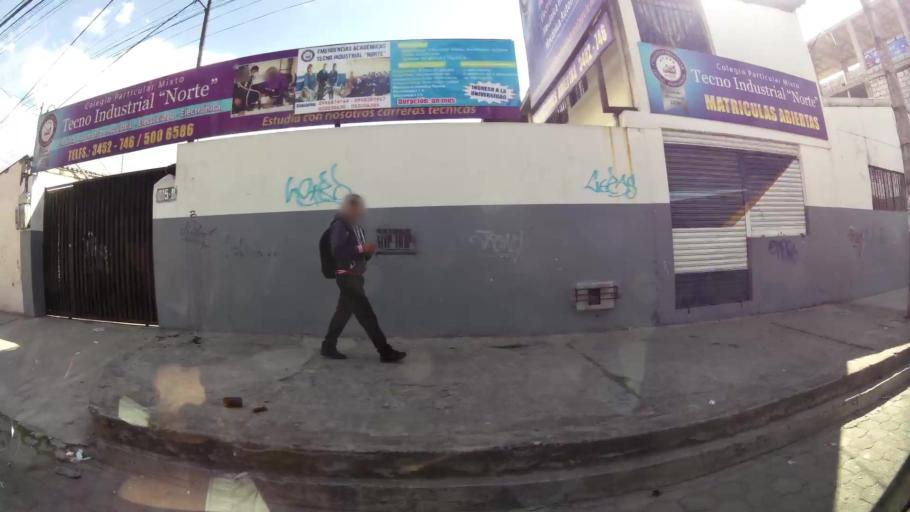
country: EC
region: Pichincha
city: Quito
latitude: -0.1261
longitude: -78.4701
